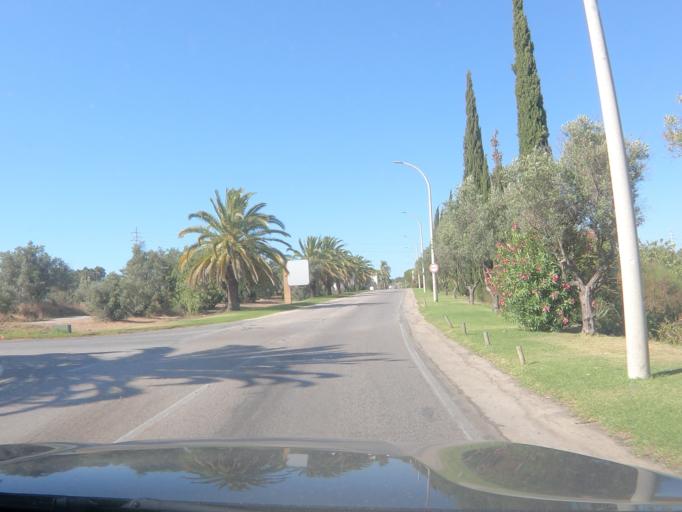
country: PT
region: Faro
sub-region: Loule
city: Vilamoura
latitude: 37.1104
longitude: -8.1202
